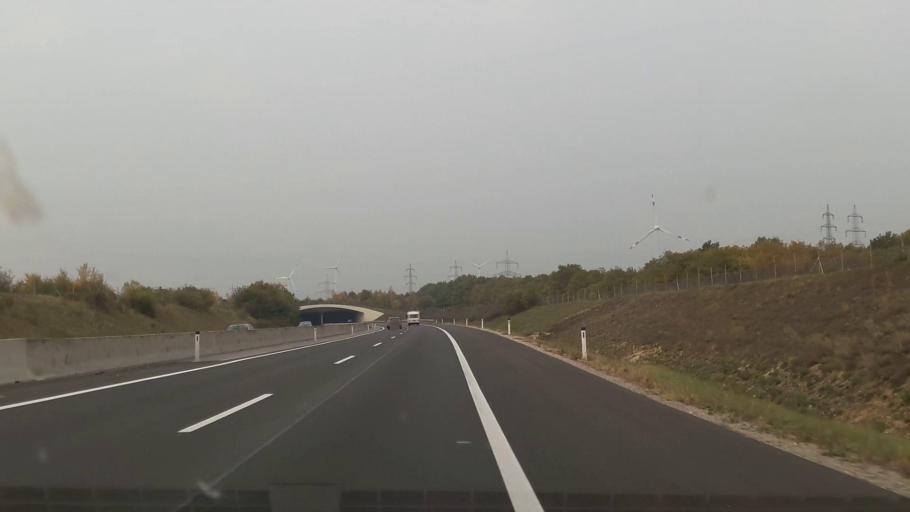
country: AT
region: Burgenland
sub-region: Politischer Bezirk Neusiedl am See
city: Weiden am See
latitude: 47.9610
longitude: 16.9101
